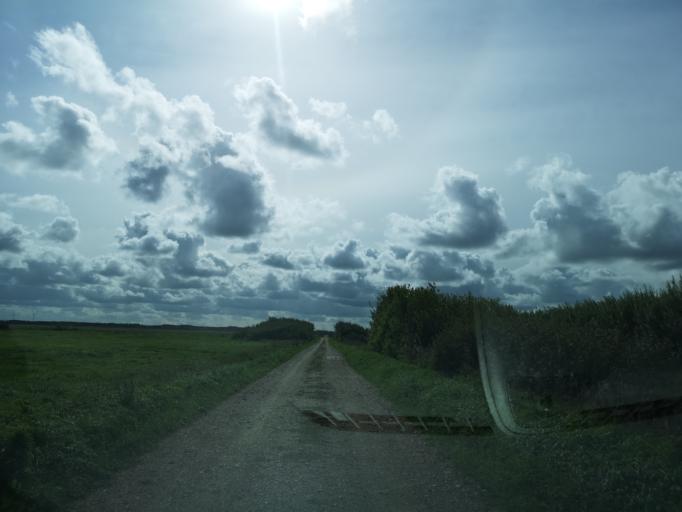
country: DK
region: Central Jutland
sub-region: Ringkobing-Skjern Kommune
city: Tarm
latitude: 55.9397
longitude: 8.5371
